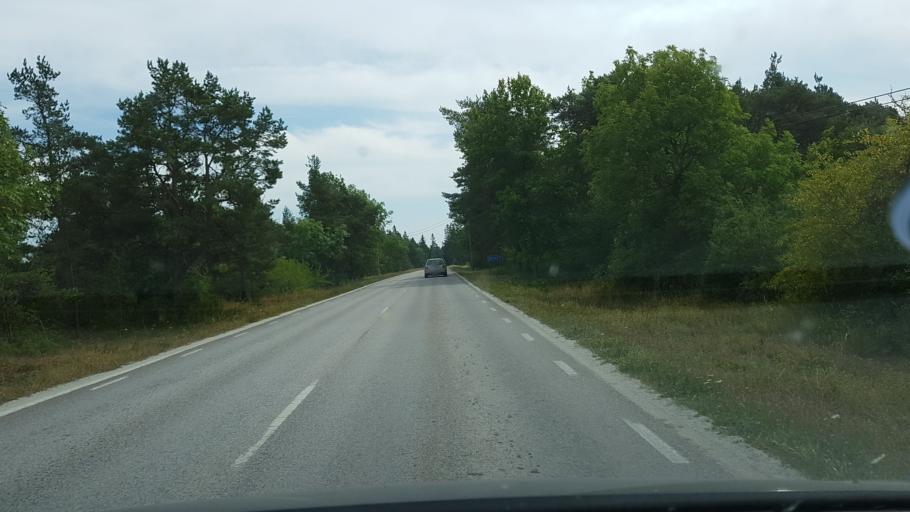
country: SE
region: Gotland
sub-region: Gotland
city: Slite
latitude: 57.7460
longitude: 18.7352
